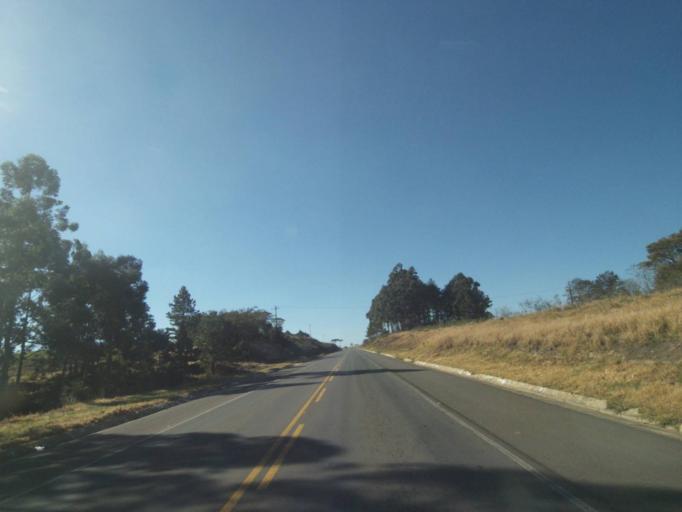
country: BR
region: Parana
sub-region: Tibagi
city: Tibagi
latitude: -24.8047
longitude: -50.4714
